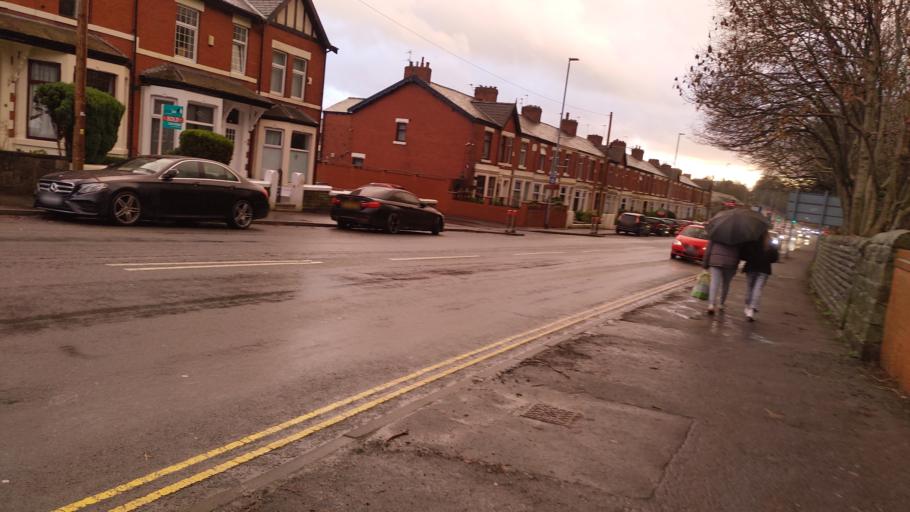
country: GB
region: England
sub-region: Blackburn with Darwen
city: Blackburn
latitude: 53.7399
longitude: -2.5085
